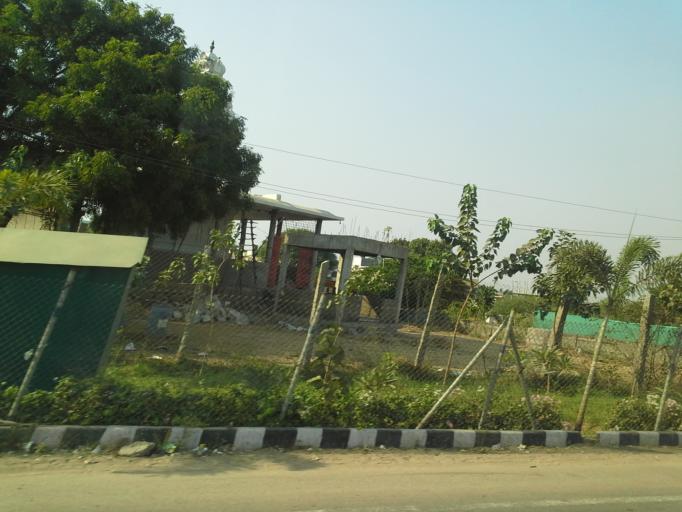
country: IN
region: Telangana
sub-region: Rangareddi
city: Balapur
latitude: 17.2678
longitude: 78.3950
